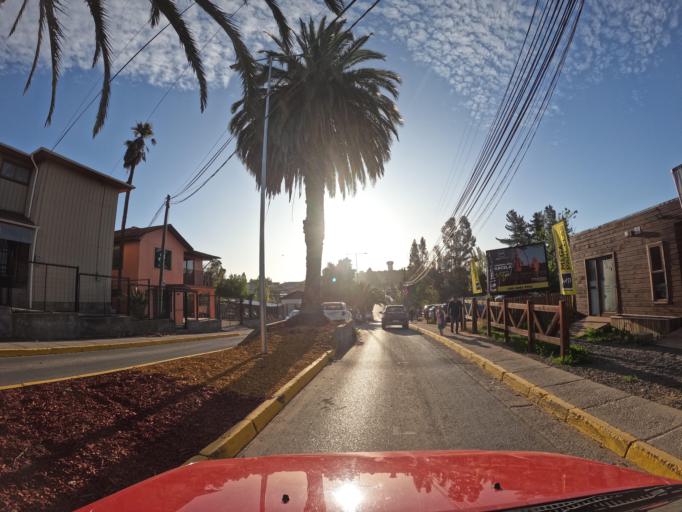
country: CL
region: Valparaiso
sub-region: San Antonio Province
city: San Antonio
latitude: -34.1171
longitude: -71.7272
